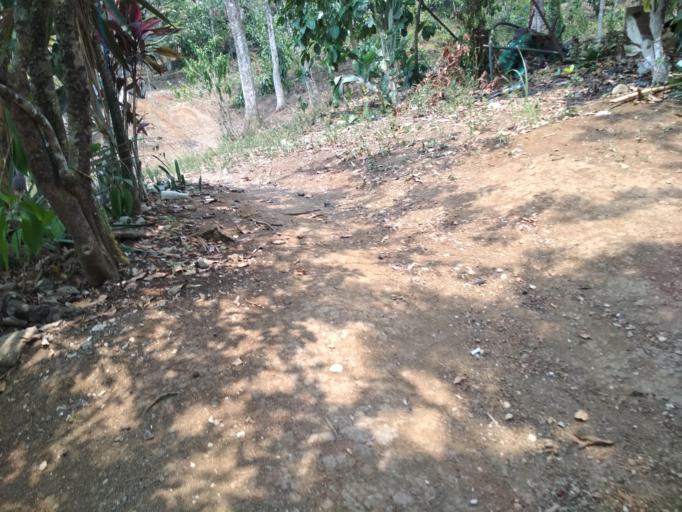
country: MX
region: Veracruz
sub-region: Tezonapa
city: Laguna Chica (Pueblo Nuevo)
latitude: 18.5469
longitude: -96.7339
